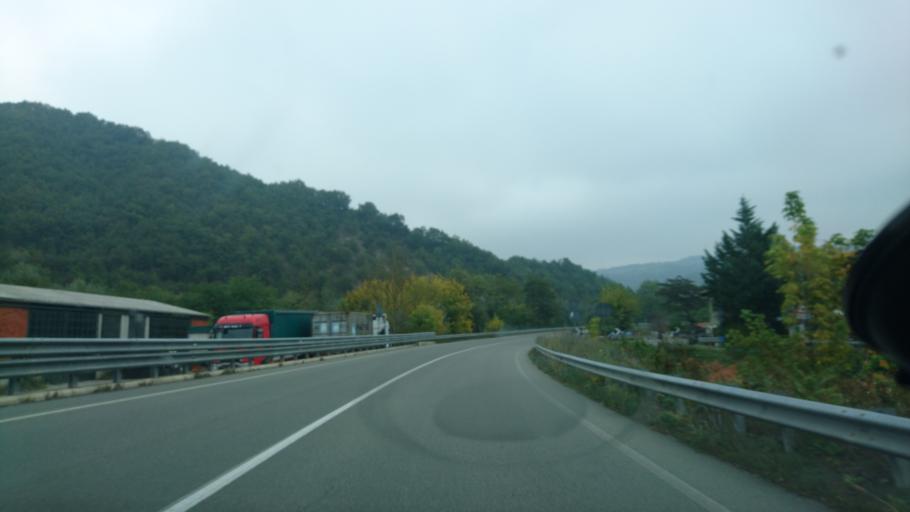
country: IT
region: Piedmont
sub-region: Provincia di Alessandria
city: Ponti
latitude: 44.6232
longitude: 8.3539
